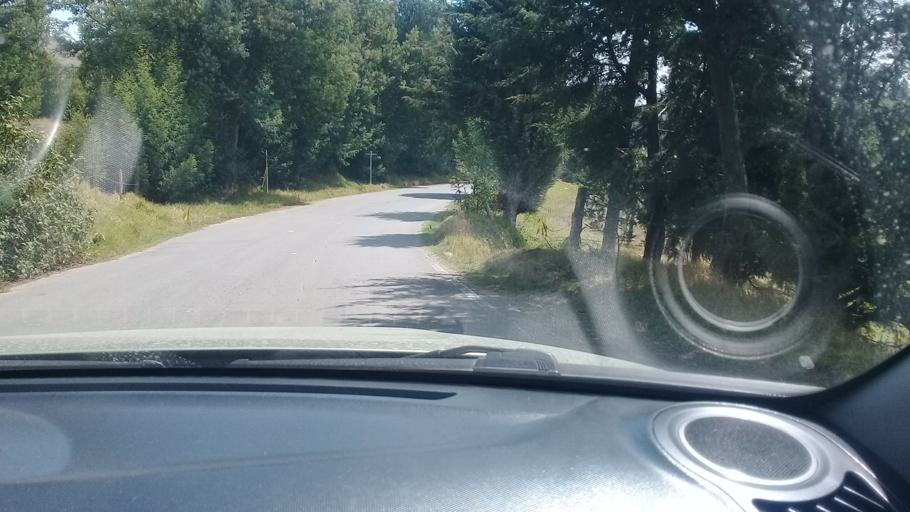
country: CO
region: Boyaca
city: Siachoque
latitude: 5.5559
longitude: -73.2843
